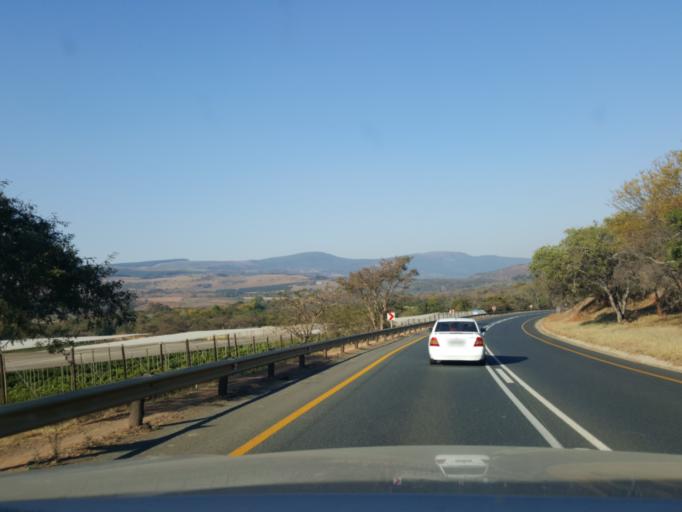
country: ZA
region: Mpumalanga
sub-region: Ehlanzeni District
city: Lydenburg
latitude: -25.3858
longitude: 30.5436
